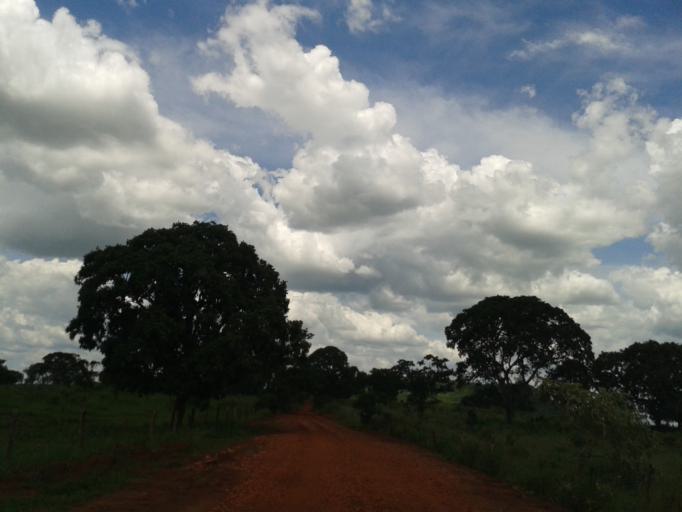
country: BR
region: Minas Gerais
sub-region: Ituiutaba
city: Ituiutaba
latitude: -18.8477
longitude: -49.5127
